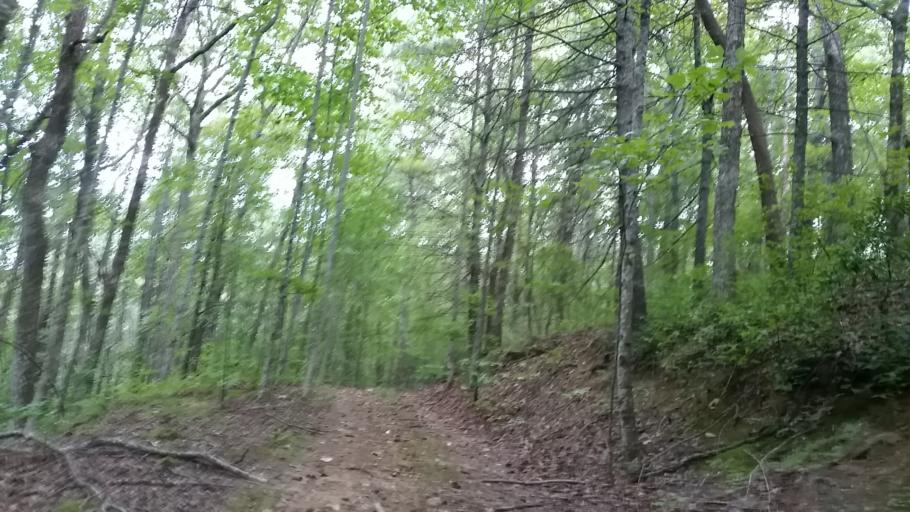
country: US
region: Georgia
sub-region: Lumpkin County
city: Dahlonega
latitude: 34.6511
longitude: -84.0628
